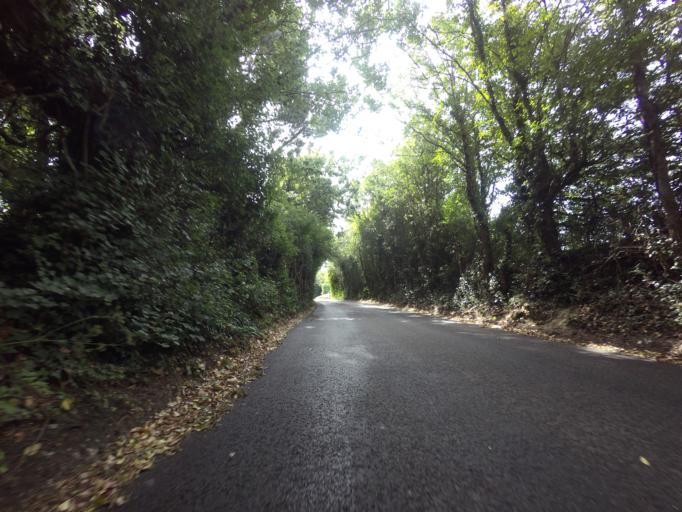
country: GB
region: England
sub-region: Kent
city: Halstead
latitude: 51.3526
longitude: 0.1390
